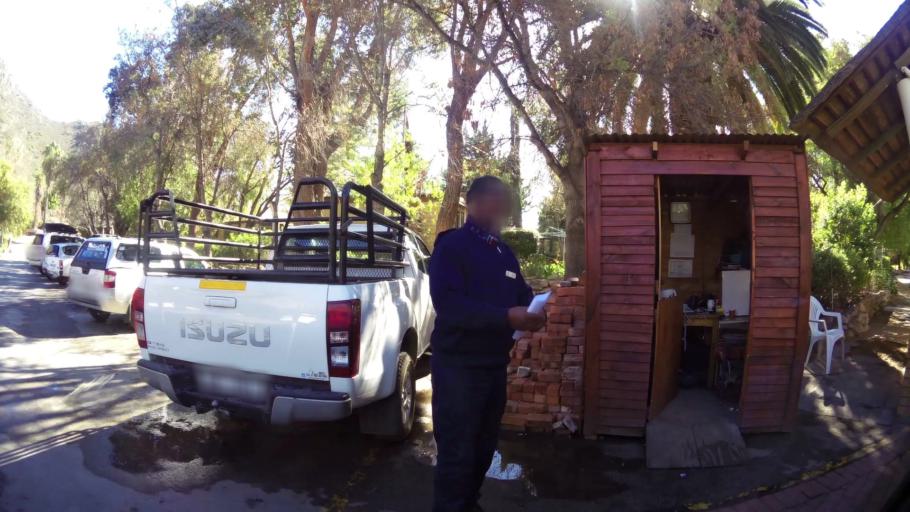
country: ZA
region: Western Cape
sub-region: Cape Winelands District Municipality
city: Ashton
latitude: -33.7655
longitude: 20.1173
